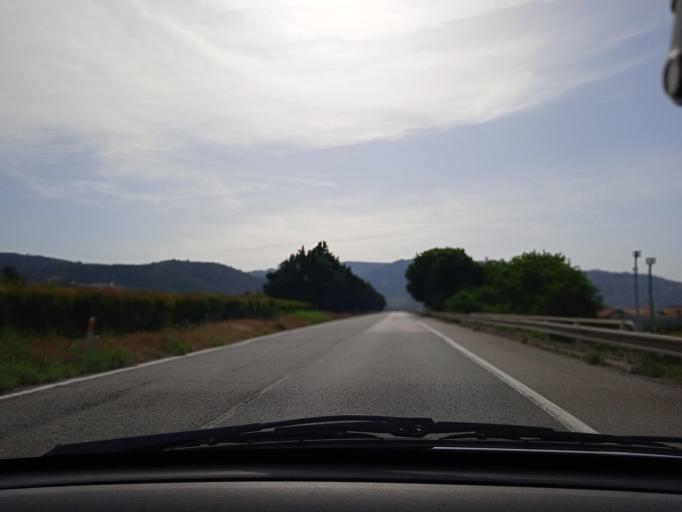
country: IT
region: Sicily
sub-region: Messina
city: Falcone
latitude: 38.1138
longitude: 15.0891
